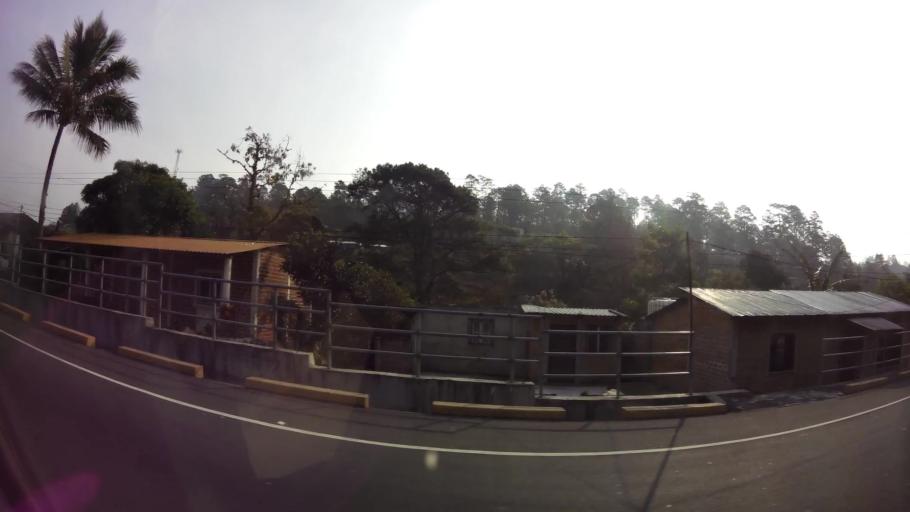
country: HN
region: Francisco Morazan
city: Zambrano
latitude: 14.2722
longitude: -87.4042
